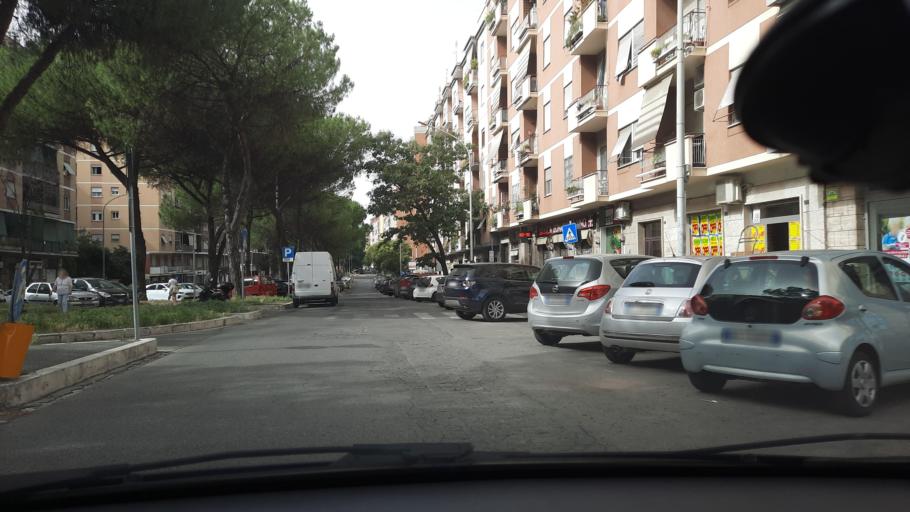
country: IT
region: Latium
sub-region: Citta metropolitana di Roma Capitale
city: Rome
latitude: 41.8545
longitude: 12.4806
